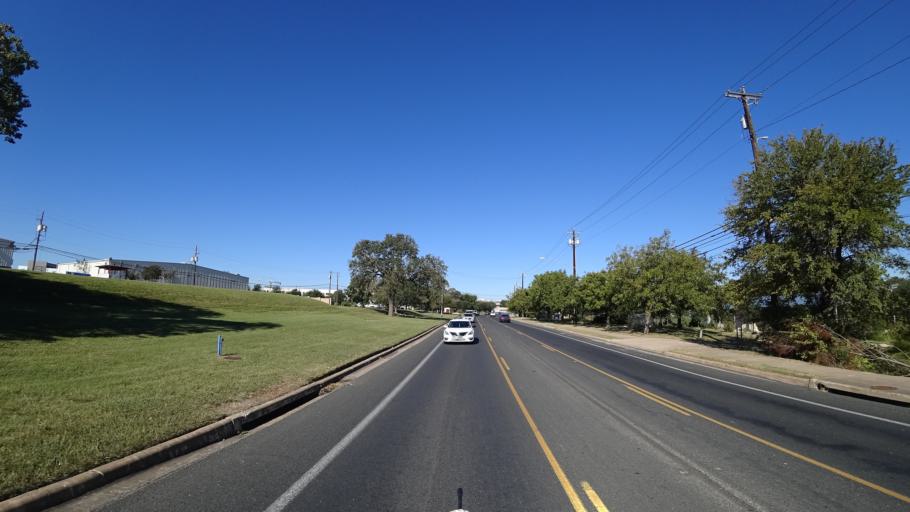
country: US
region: Texas
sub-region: Travis County
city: Austin
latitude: 30.3018
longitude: -97.6962
